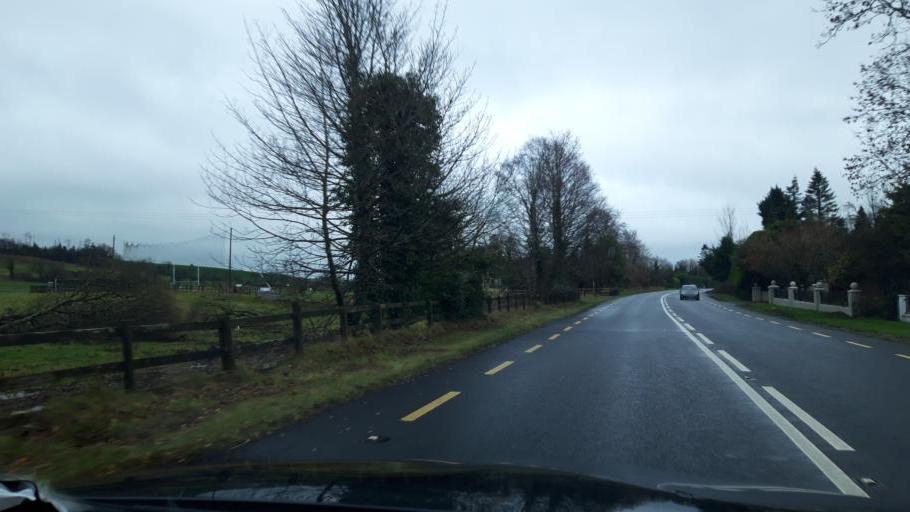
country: IE
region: Ulster
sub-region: County Monaghan
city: Castleblayney
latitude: 54.1063
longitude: -6.7147
